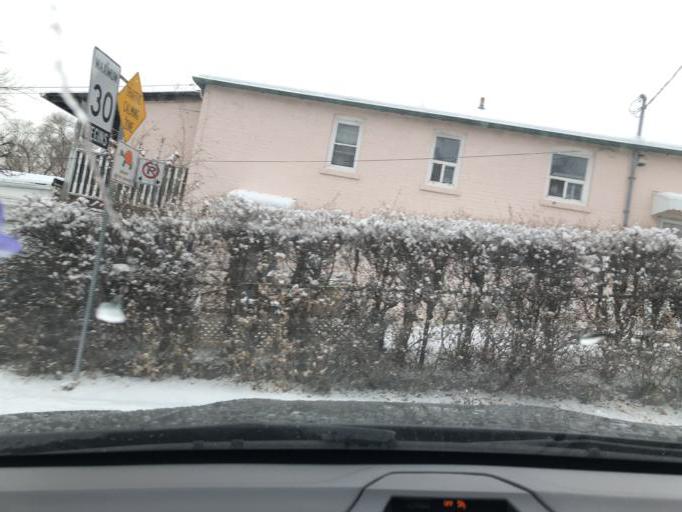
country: CA
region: Ontario
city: Toronto
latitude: 43.6903
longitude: -79.4702
